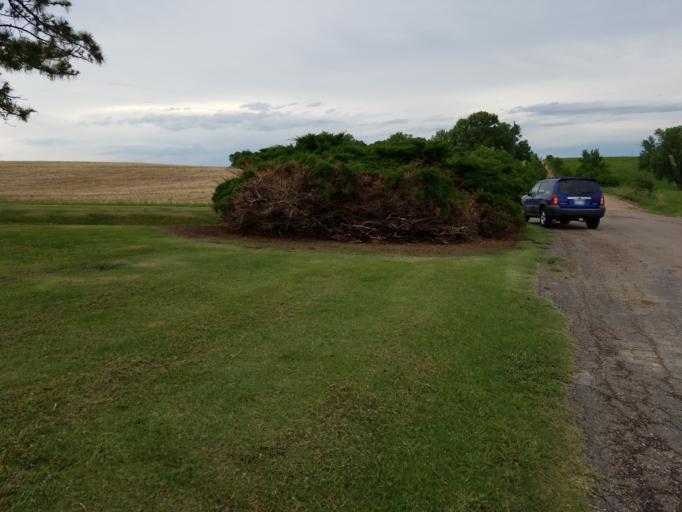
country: US
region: Kansas
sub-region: Smith County
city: Smith Center
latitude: 39.8283
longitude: -98.5794
